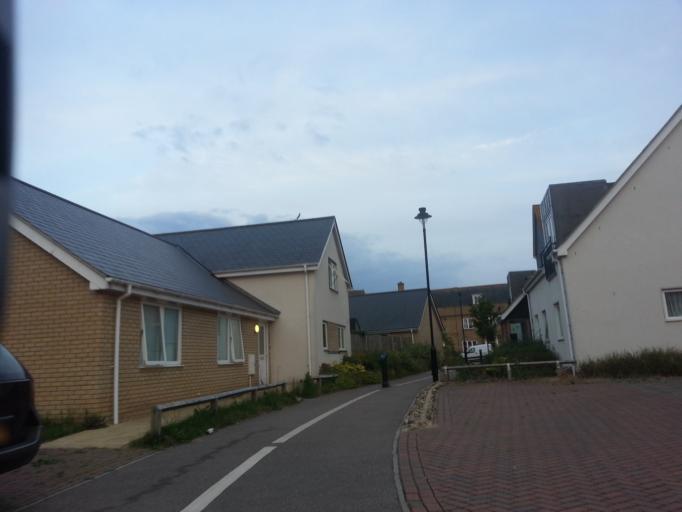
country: GB
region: England
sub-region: Suffolk
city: Kesgrave
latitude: 52.0301
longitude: 1.1991
